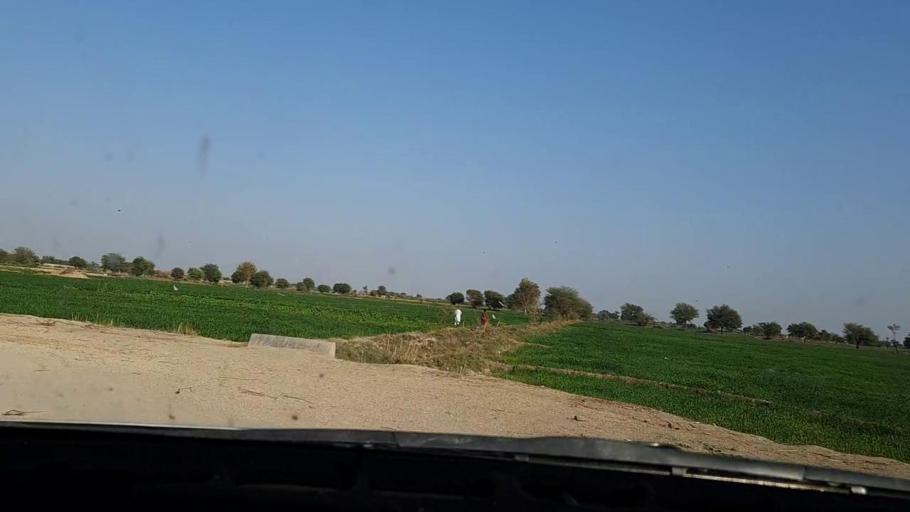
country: PK
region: Sindh
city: Tando Mittha Khan
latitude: 25.8283
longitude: 69.3124
